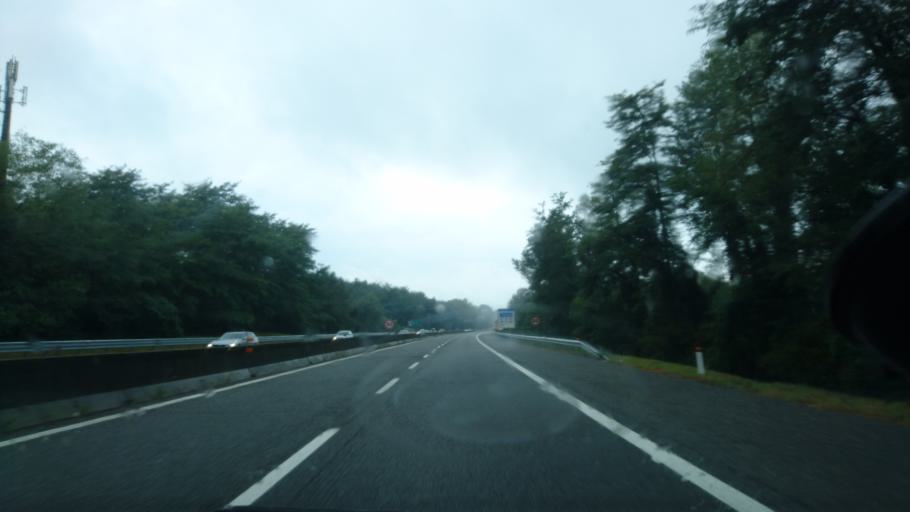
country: IT
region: Piedmont
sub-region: Provincia di Novara
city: Paruzzaro
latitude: 45.7342
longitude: 8.5075
